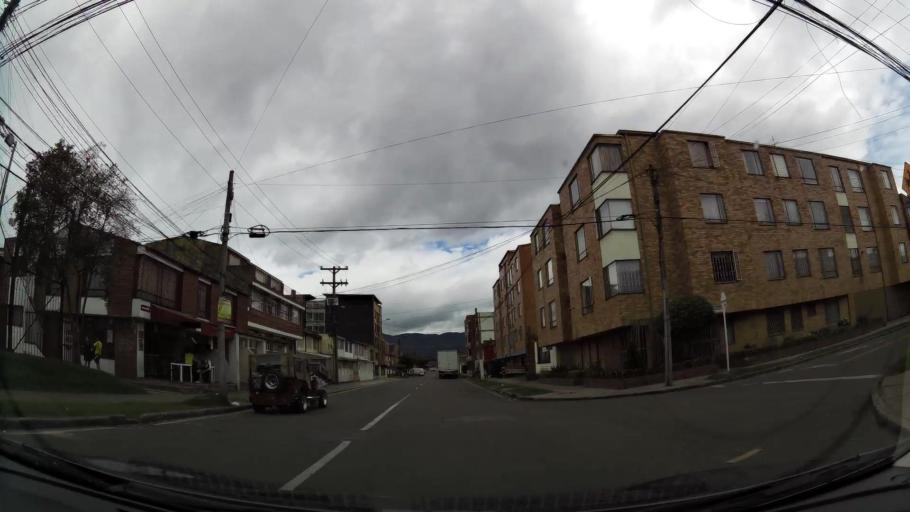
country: CO
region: Bogota D.C.
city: Barrio San Luis
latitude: 4.6902
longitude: -74.0968
